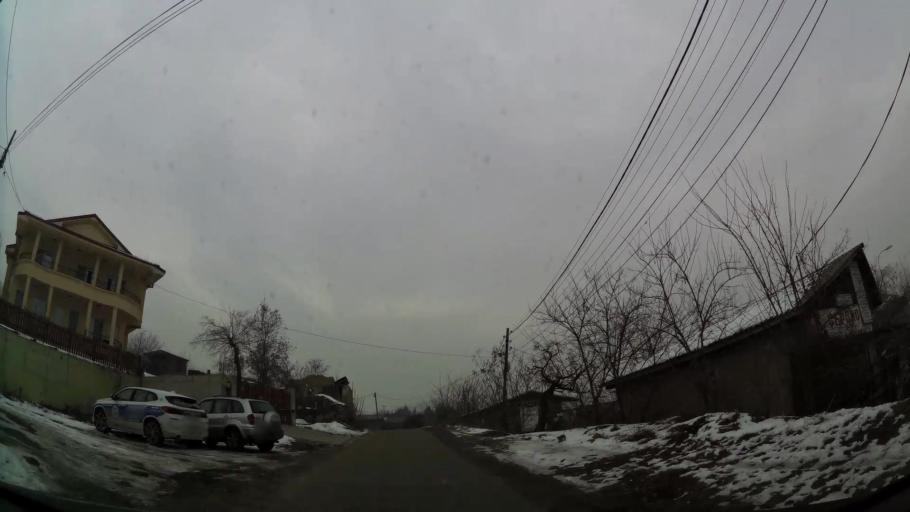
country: MK
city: Kondovo
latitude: 42.0464
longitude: 21.3458
